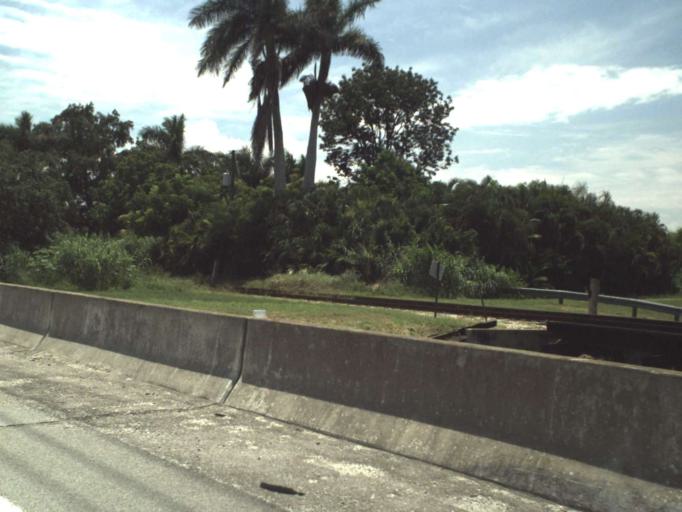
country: US
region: Florida
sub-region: Palm Beach County
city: Pahokee
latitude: 26.9172
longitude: -80.6133
